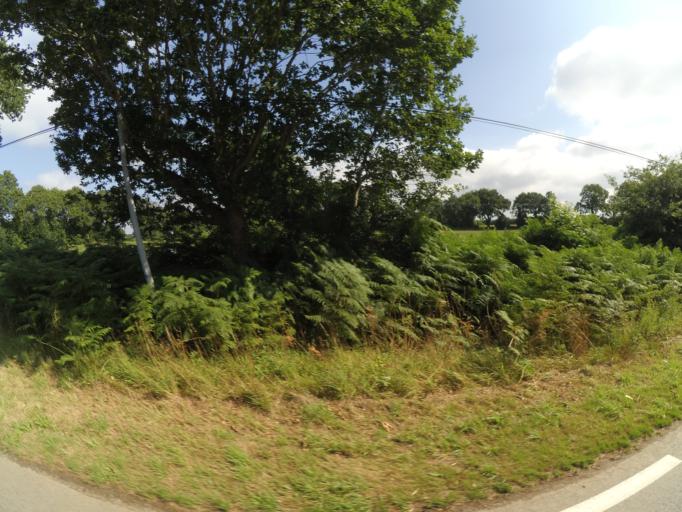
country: FR
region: Brittany
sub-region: Departement du Finistere
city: Le Trevoux
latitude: 47.9192
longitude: -3.6235
